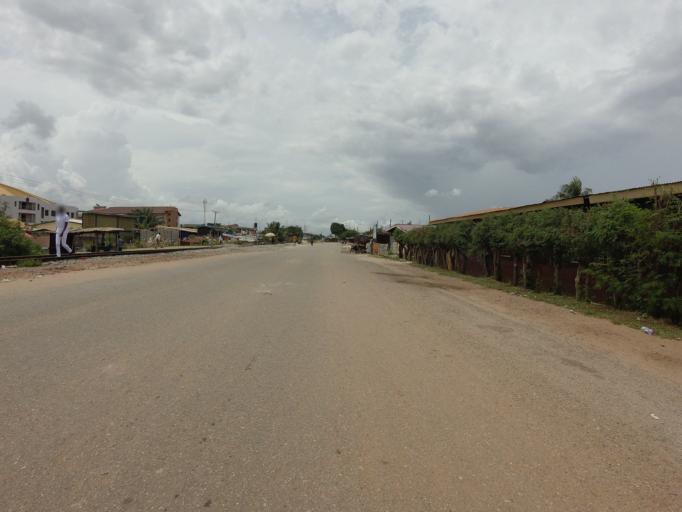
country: GH
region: Greater Accra
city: Accra
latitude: 5.6056
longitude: -0.2088
